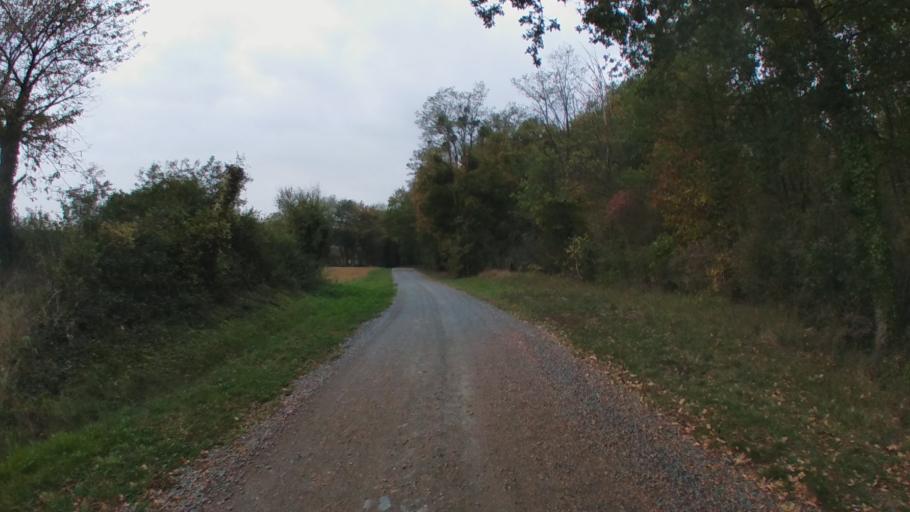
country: FR
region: Pays de la Loire
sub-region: Departement de Maine-et-Loire
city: Distre
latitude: 47.2422
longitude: -0.1240
